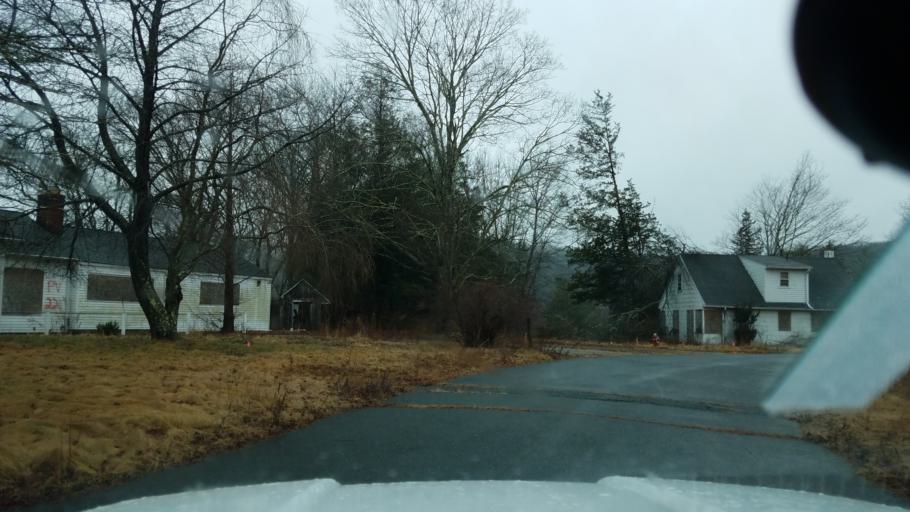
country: US
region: Connecticut
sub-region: New Haven County
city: Heritage Village
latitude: 41.4869
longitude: -73.2564
